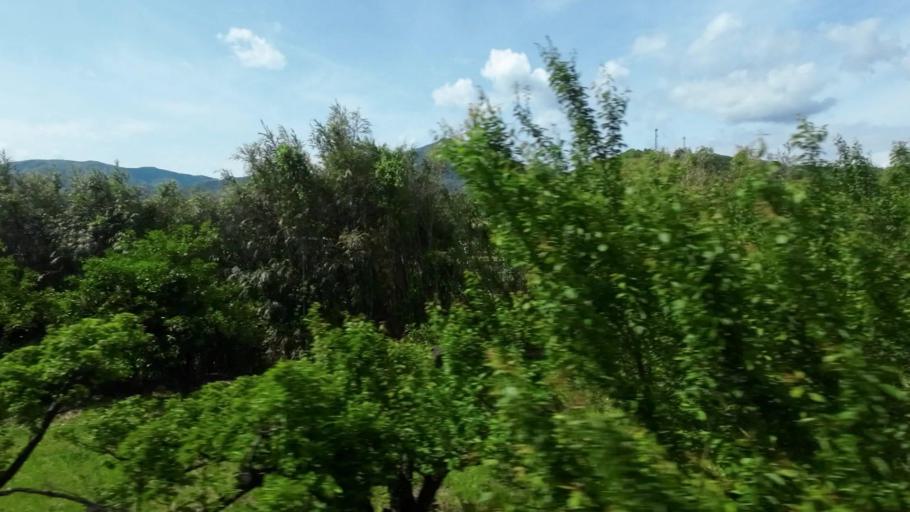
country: JP
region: Tokushima
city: Wakimachi
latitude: 34.0571
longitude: 134.2219
